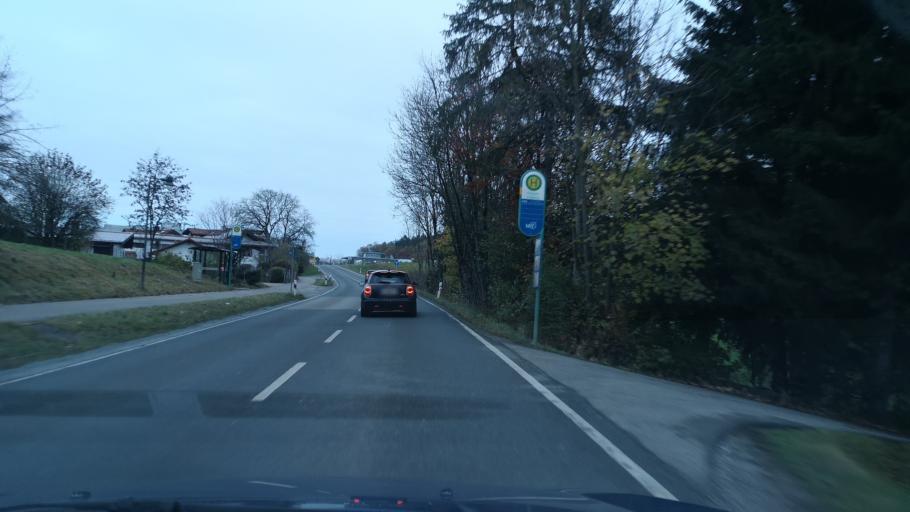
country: DE
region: Bavaria
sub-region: Upper Bavaria
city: Ebersberg
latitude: 48.0920
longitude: 11.9658
